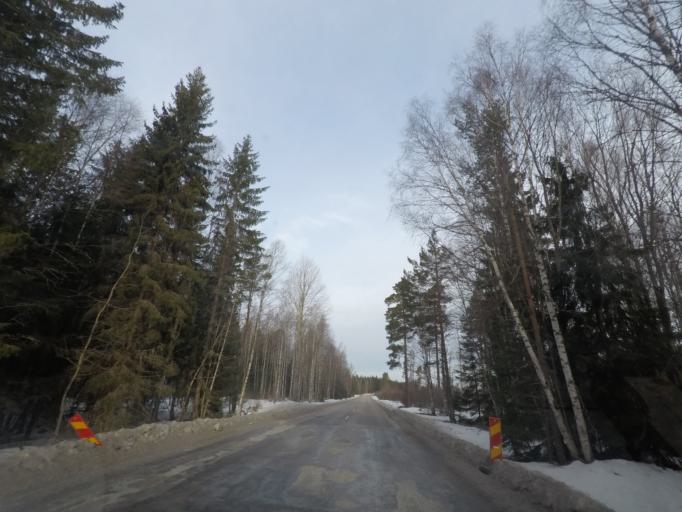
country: SE
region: Vaestmanland
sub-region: Surahammars Kommun
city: Surahammar
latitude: 59.7564
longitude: 16.3083
